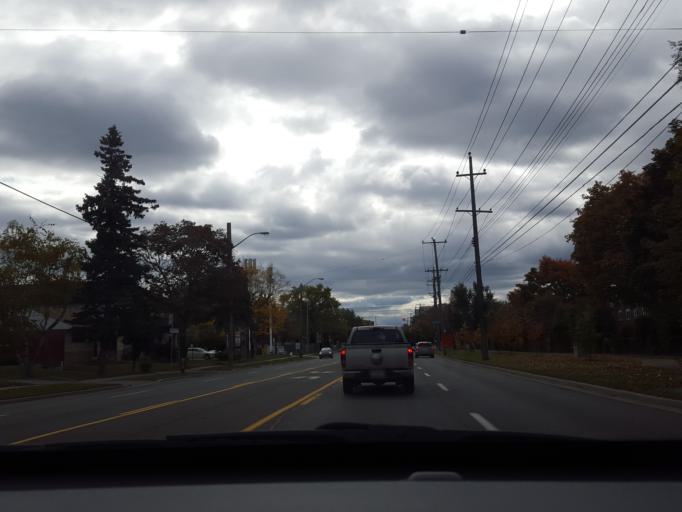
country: CA
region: Ontario
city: Scarborough
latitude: 43.7971
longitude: -79.2944
